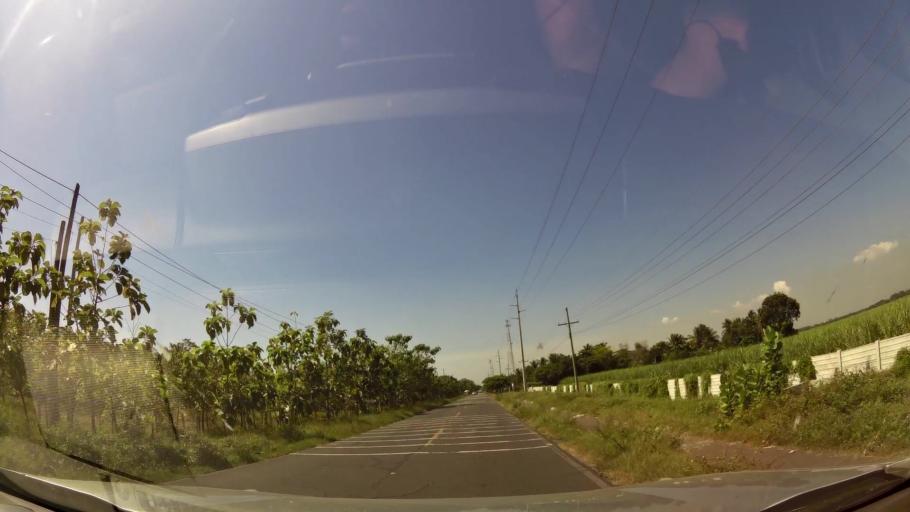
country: GT
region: Escuintla
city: Iztapa
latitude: 13.9340
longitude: -90.7593
